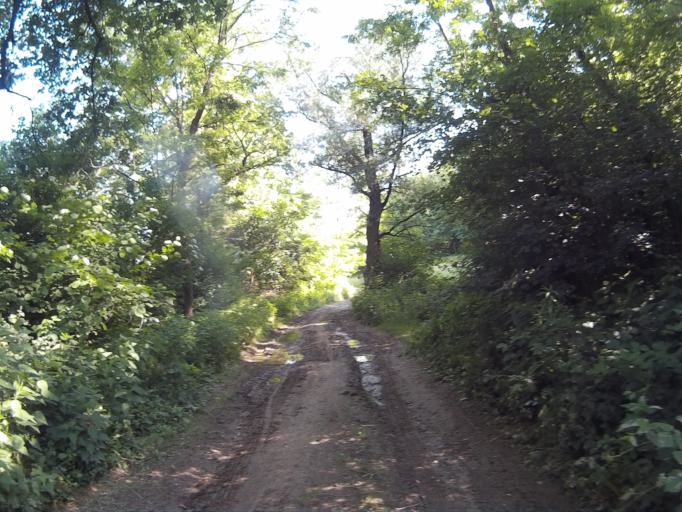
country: AT
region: Burgenland
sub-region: Politischer Bezirk Gussing
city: Heiligenbrunn
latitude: 46.9349
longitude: 16.4710
